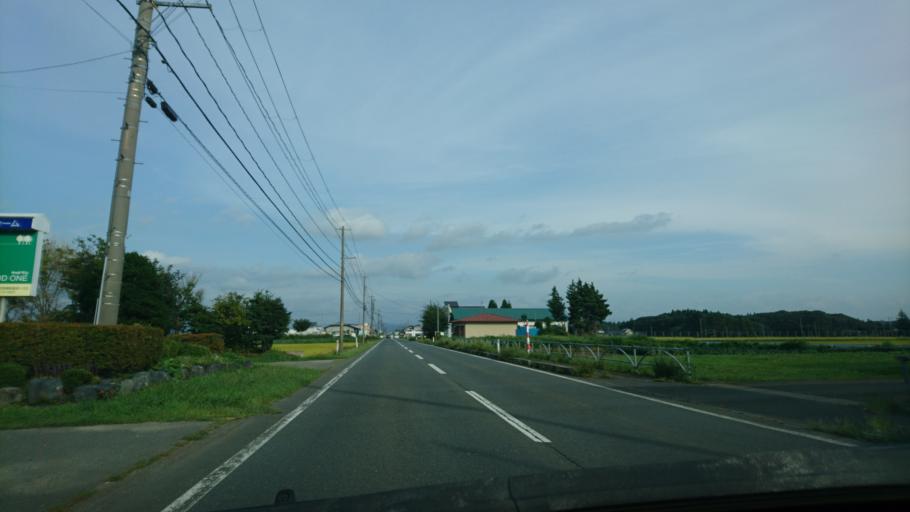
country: JP
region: Iwate
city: Kitakami
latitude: 39.3053
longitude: 141.0098
